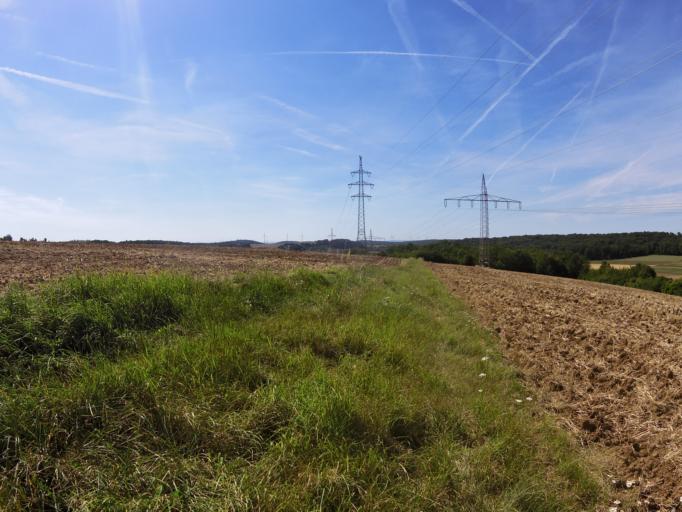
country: DE
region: Bavaria
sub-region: Regierungsbezirk Unterfranken
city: Hettstadt
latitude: 49.8135
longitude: 9.8251
